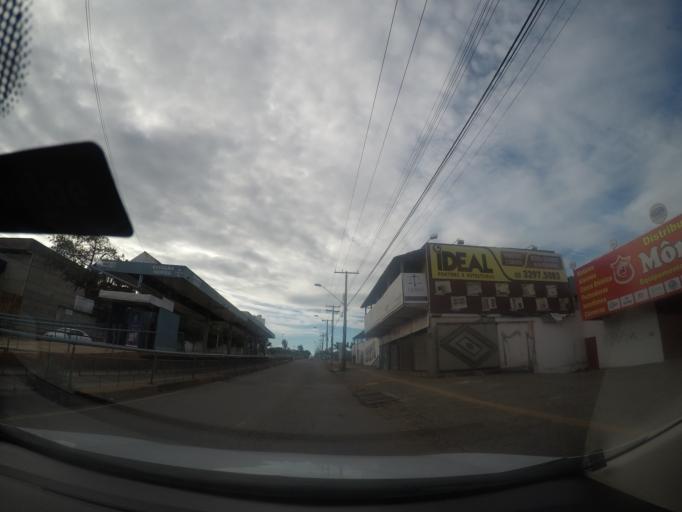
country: BR
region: Goias
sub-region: Goiania
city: Goiania
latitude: -16.6618
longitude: -49.3238
